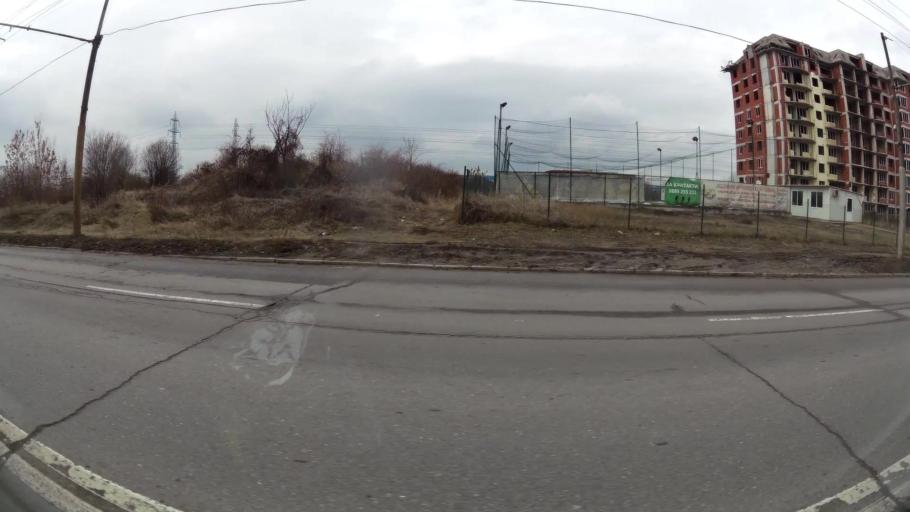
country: BG
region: Sofiya
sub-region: Obshtina Bozhurishte
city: Bozhurishte
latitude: 42.7268
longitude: 23.2458
